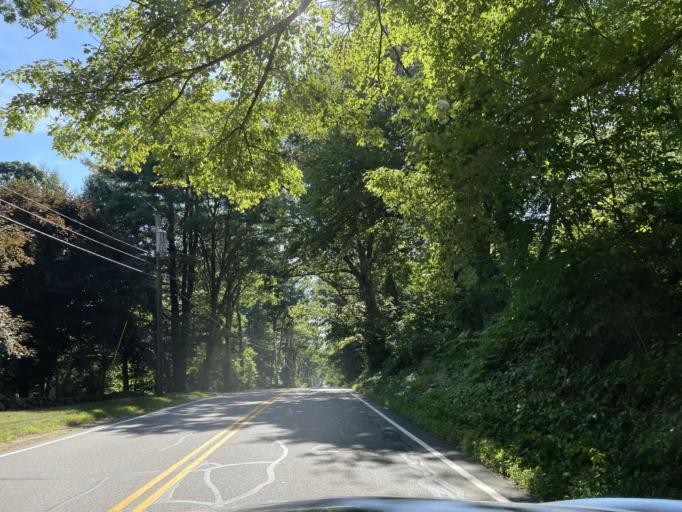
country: US
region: Massachusetts
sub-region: Worcester County
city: Northbridge
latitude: 42.1533
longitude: -71.6973
